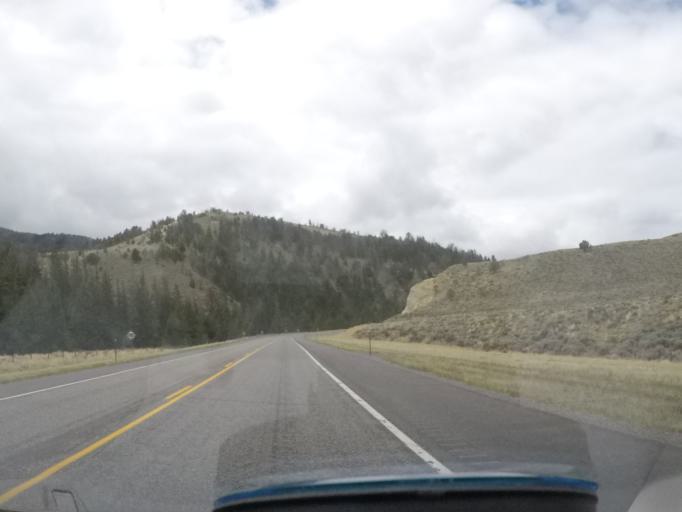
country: US
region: Wyoming
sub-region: Sublette County
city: Pinedale
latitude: 43.5789
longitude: -109.7566
